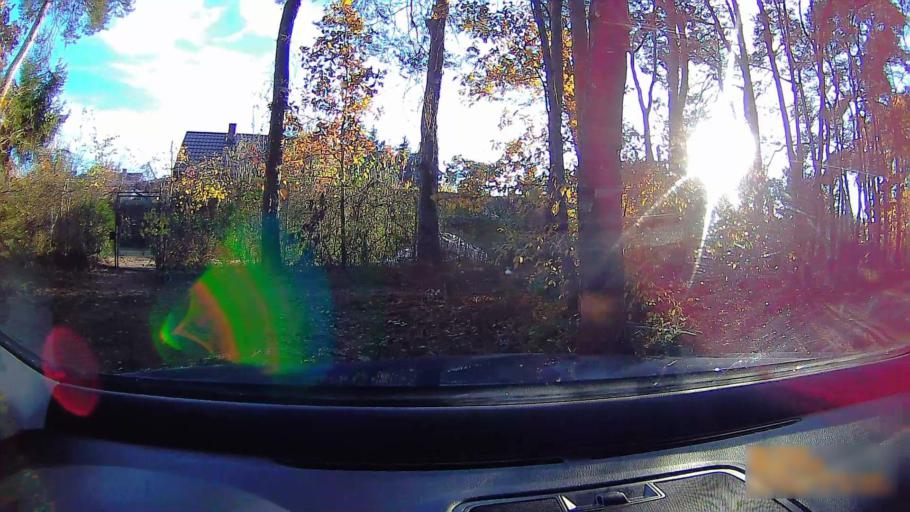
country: PL
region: Greater Poland Voivodeship
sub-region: Powiat koninski
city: Stare Miasto
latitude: 52.2039
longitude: 18.2059
